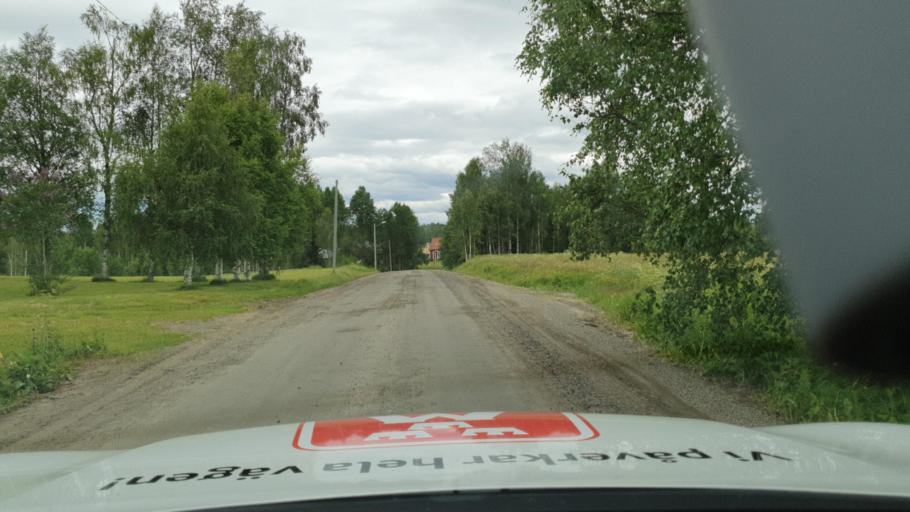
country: SE
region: Vaesterbotten
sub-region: Nordmalings Kommun
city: Nordmaling
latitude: 63.7117
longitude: 19.4303
